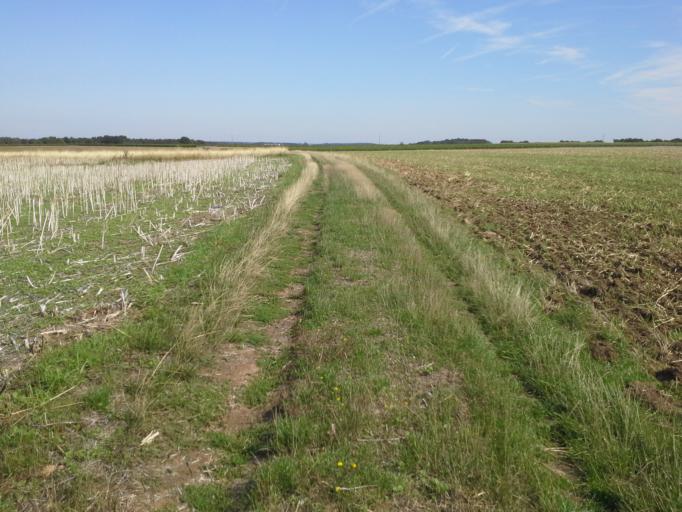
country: FR
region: Centre
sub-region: Departement du Loir-et-Cher
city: Villiers-sur-Loir
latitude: 47.8167
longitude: 0.9810
